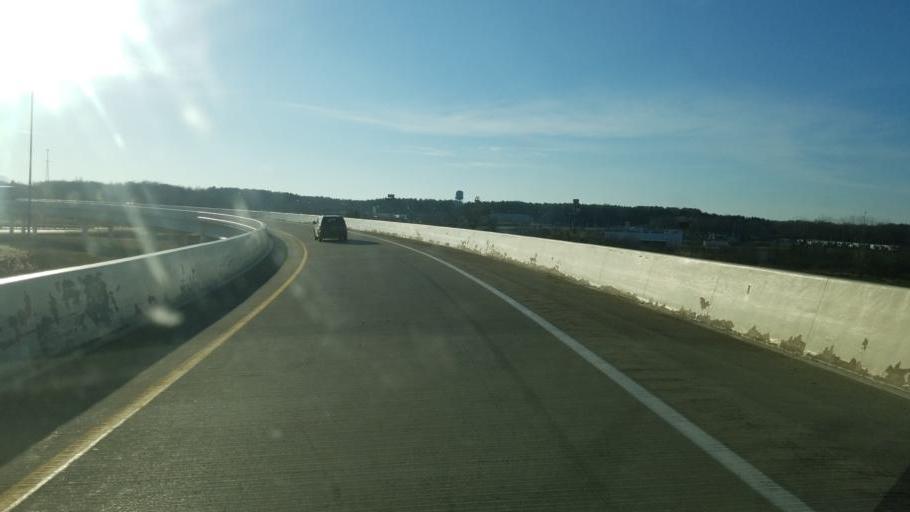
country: US
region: Ohio
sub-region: Medina County
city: Westfield Center
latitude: 41.0324
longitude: -81.8998
